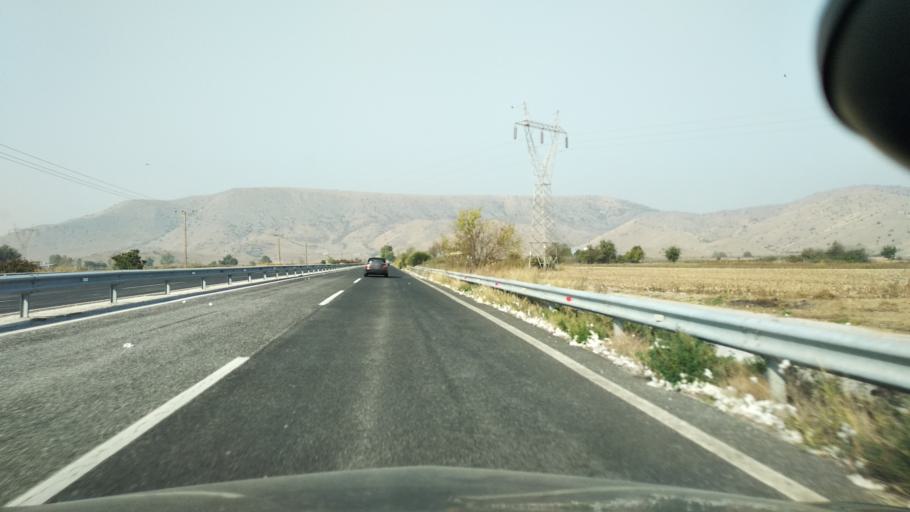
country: GR
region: Thessaly
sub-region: Trikala
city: Zarkos
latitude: 39.5964
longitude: 22.1123
